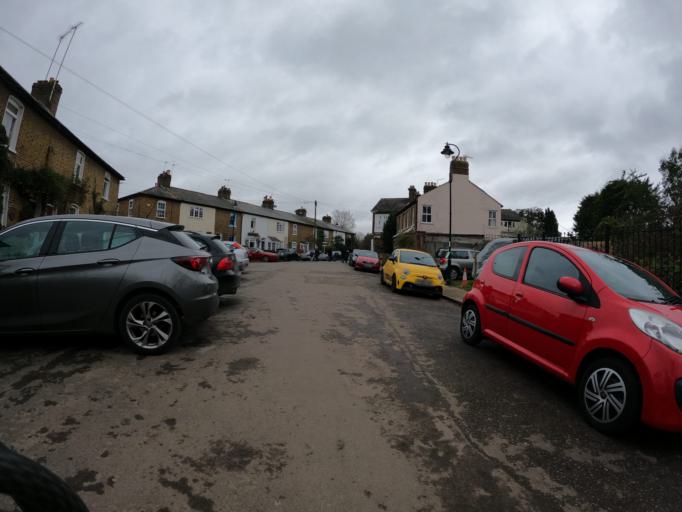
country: GB
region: England
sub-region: Greater London
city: Greenford
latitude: 51.5039
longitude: -0.3437
